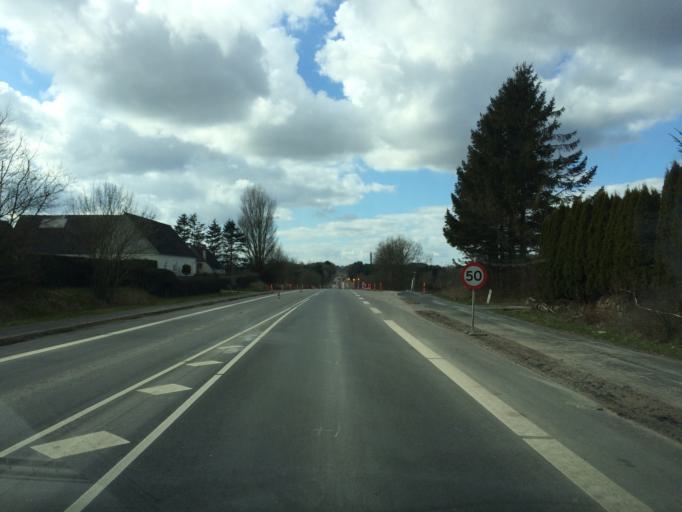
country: DK
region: South Denmark
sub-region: Assens Kommune
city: Vissenbjerg
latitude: 55.3870
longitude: 10.1784
